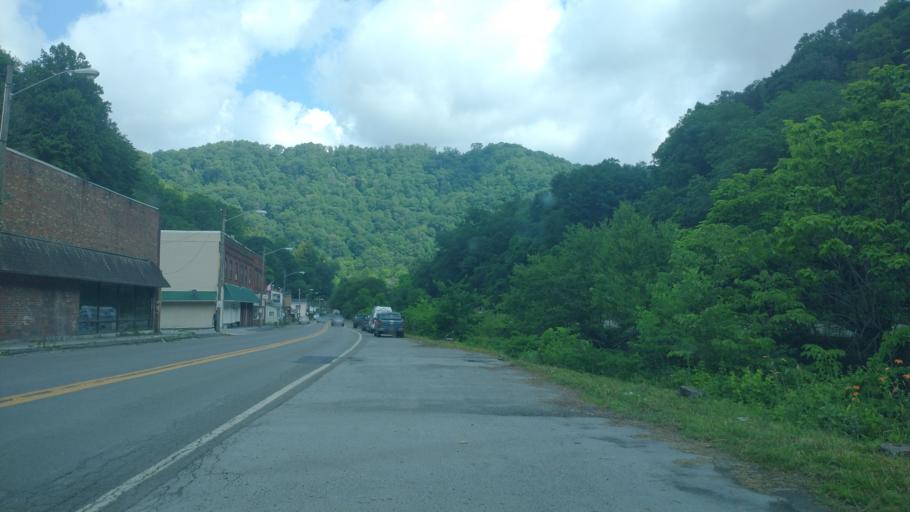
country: US
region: West Virginia
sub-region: McDowell County
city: Welch
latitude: 37.4168
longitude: -81.4369
